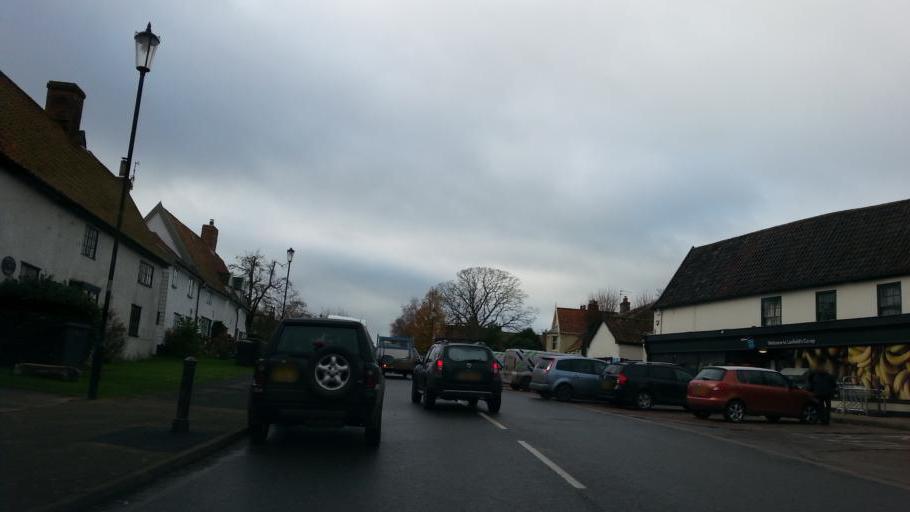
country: GB
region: England
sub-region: Suffolk
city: Framlingham
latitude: 52.3017
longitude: 1.3665
